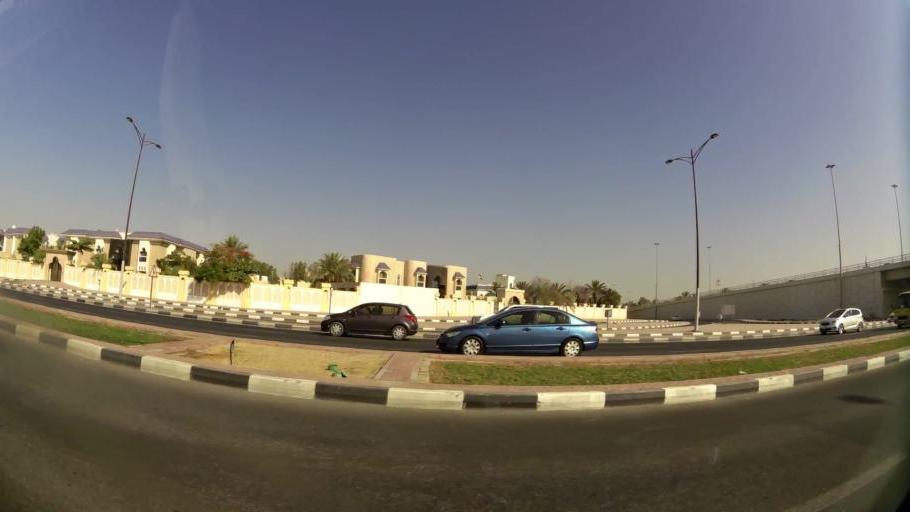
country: AE
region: Ash Shariqah
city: Sharjah
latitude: 25.3579
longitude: 55.4413
